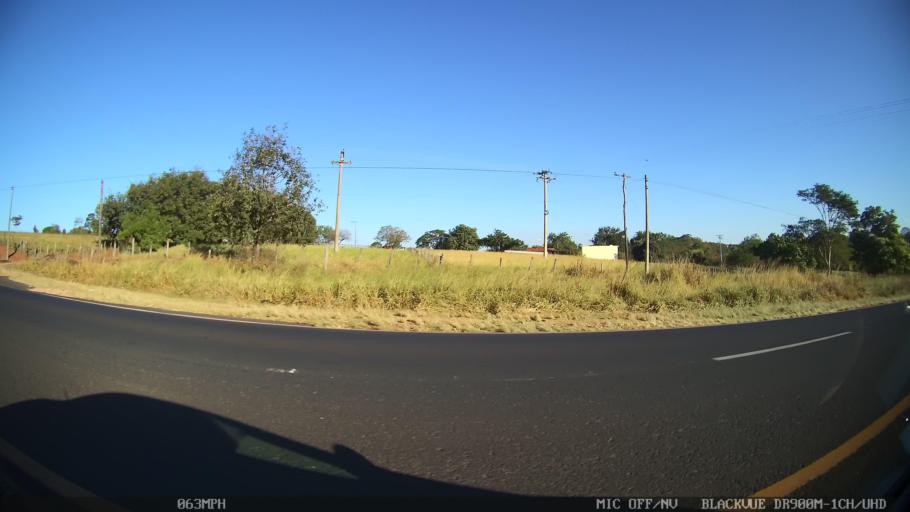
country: BR
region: Sao Paulo
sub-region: Guapiacu
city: Guapiacu
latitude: -20.7693
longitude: -49.2107
